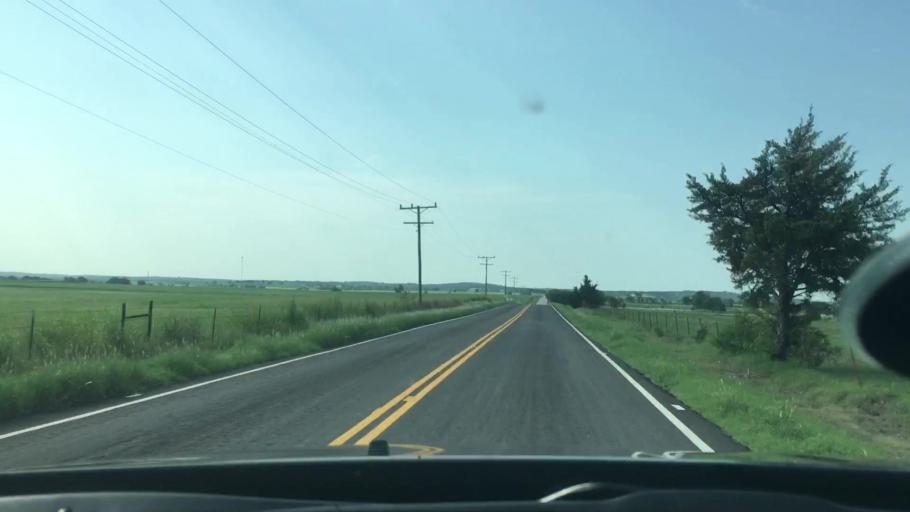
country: US
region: Oklahoma
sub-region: Bryan County
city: Durant
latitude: 34.1175
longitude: -96.4877
